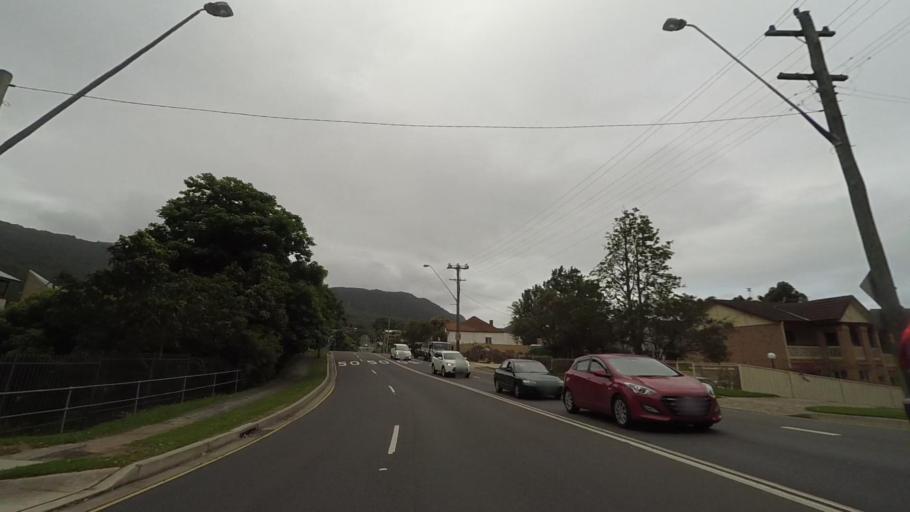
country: AU
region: New South Wales
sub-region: Wollongong
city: Bulli
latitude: -34.3192
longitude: 150.9165
